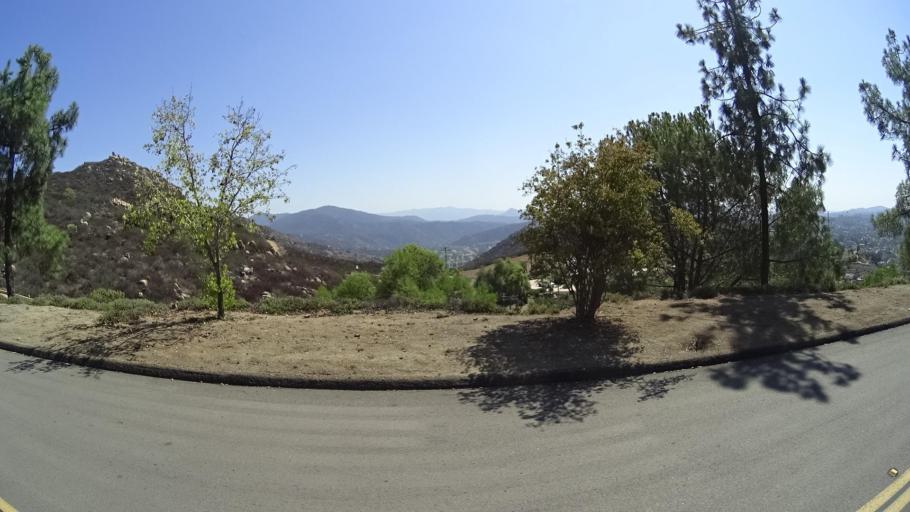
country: US
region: California
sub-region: San Diego County
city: Granite Hills
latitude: 32.8031
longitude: -116.8903
